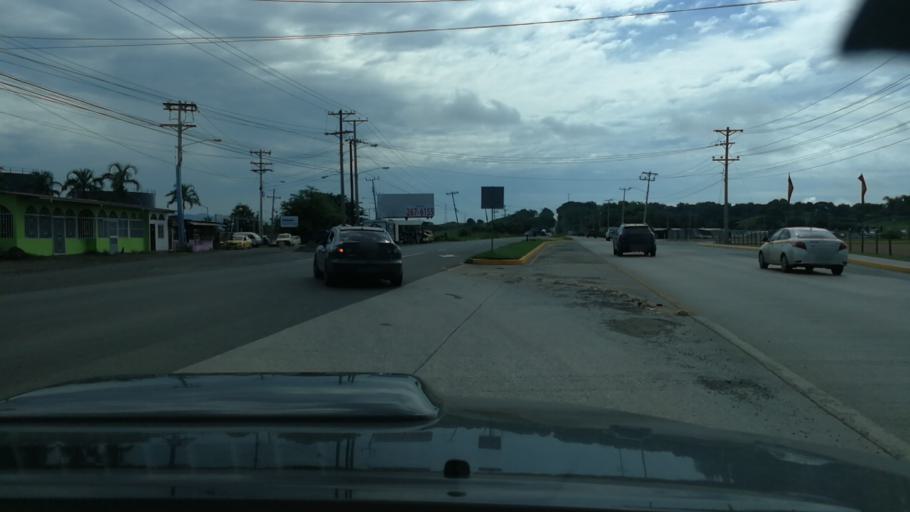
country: PA
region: Panama
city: Los Lotes
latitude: 9.1036
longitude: -79.2732
